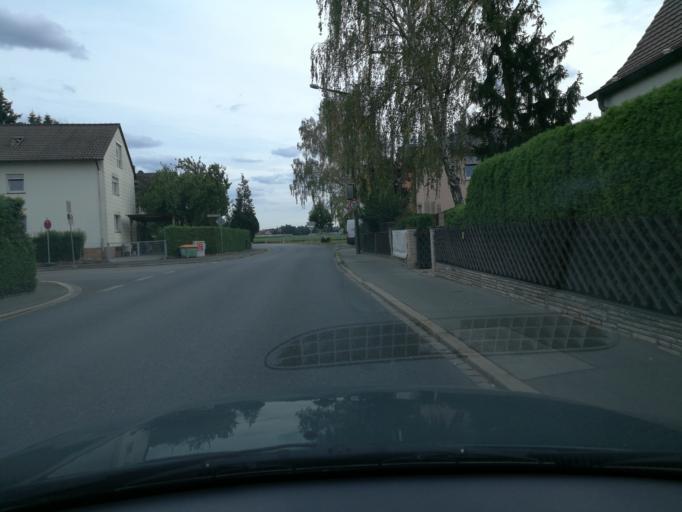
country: DE
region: Bavaria
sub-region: Regierungsbezirk Mittelfranken
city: Furth
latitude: 49.5070
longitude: 11.0046
